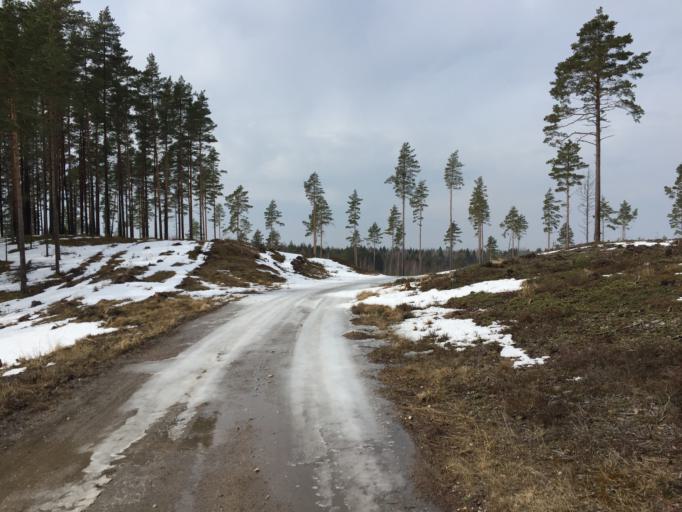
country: EE
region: Saare
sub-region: Kuressaare linn
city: Kuressaare
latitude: 58.3955
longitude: 22.1703
